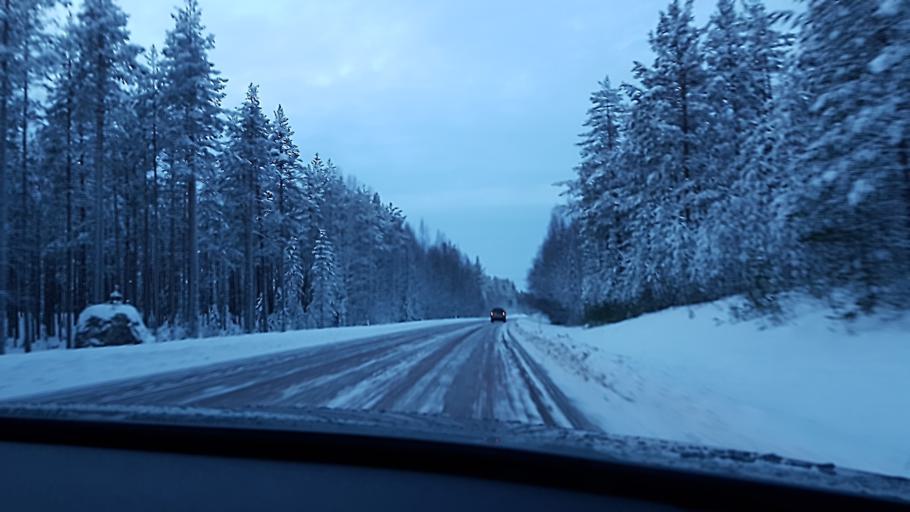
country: SE
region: Jaemtland
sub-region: Harjedalens Kommun
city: Sveg
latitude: 62.0447
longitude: 14.8574
